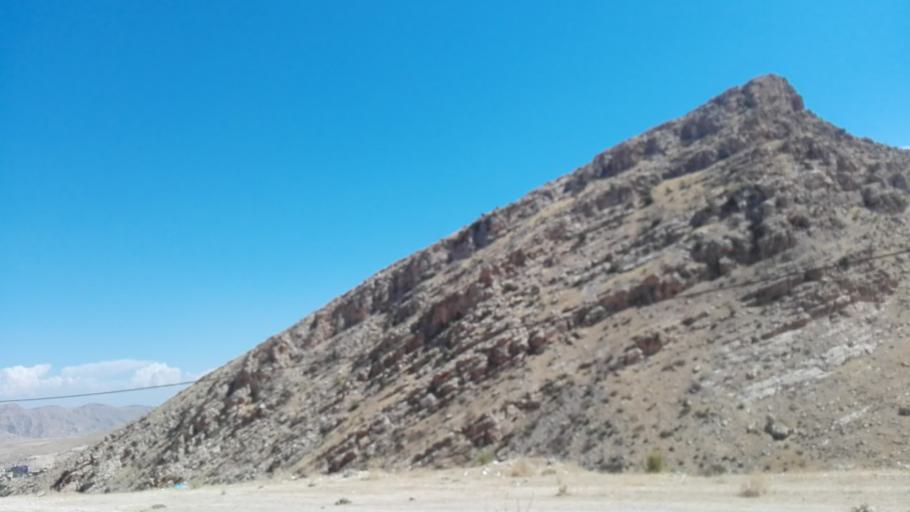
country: TR
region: Batman
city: Hasankeyf
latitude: 37.6996
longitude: 41.4591
